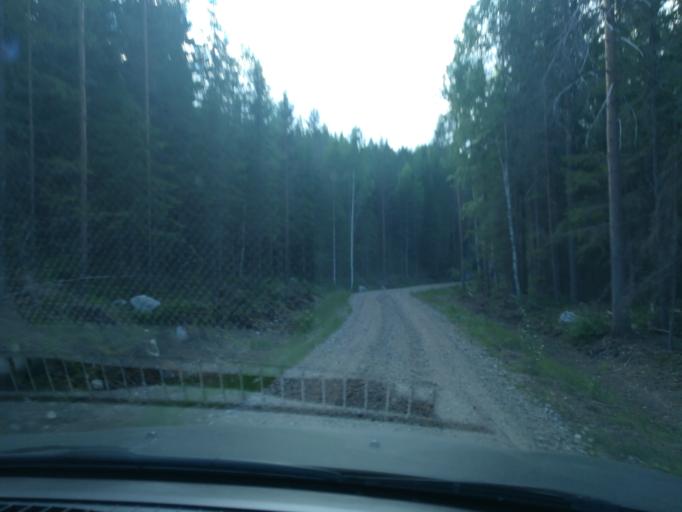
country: FI
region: Southern Savonia
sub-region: Mikkeli
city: Puumala
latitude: 61.6253
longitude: 28.1697
